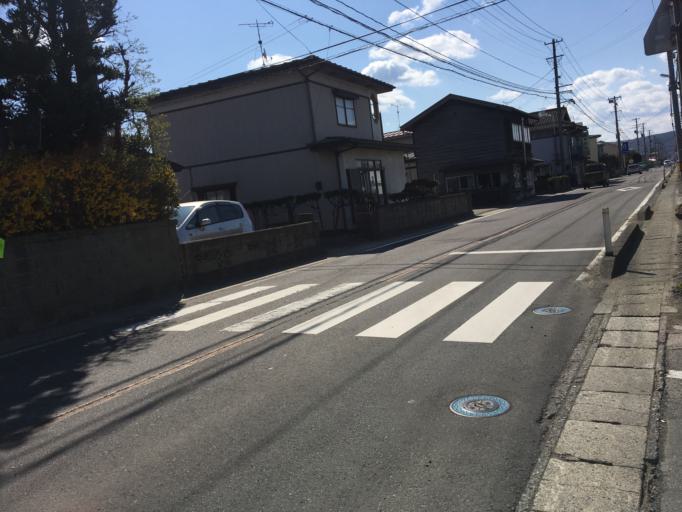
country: JP
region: Aomori
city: Hachinohe
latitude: 40.2085
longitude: 141.7933
